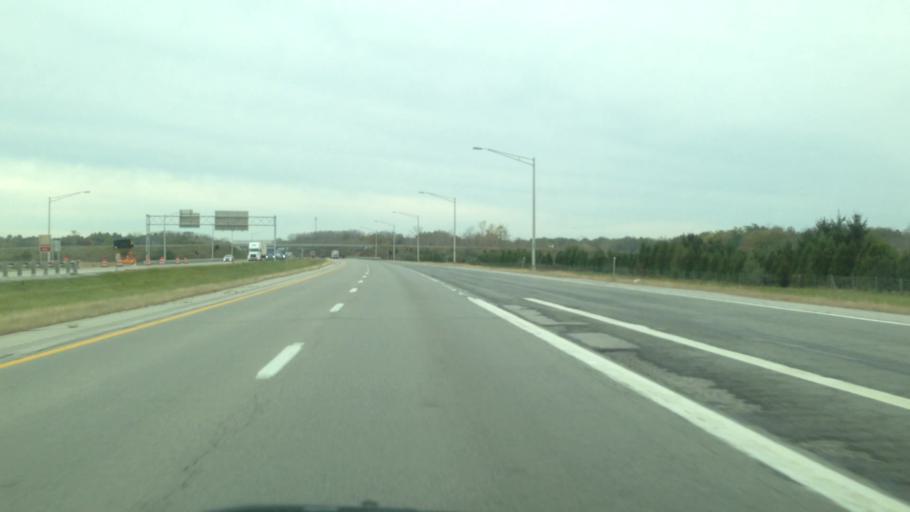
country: US
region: Ohio
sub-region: Fulton County
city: Burlington
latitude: 41.5917
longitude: -84.3209
